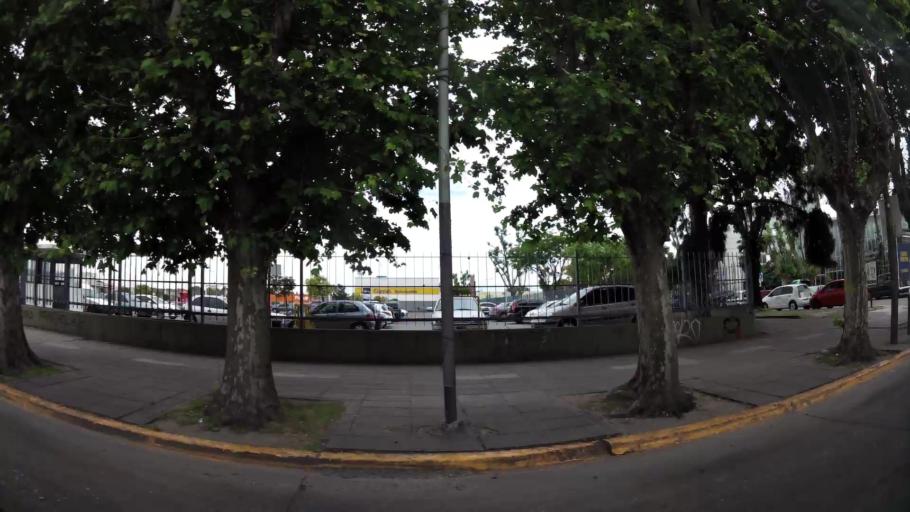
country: AR
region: Buenos Aires
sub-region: Partido de Avellaneda
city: Avellaneda
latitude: -34.6755
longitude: -58.3647
